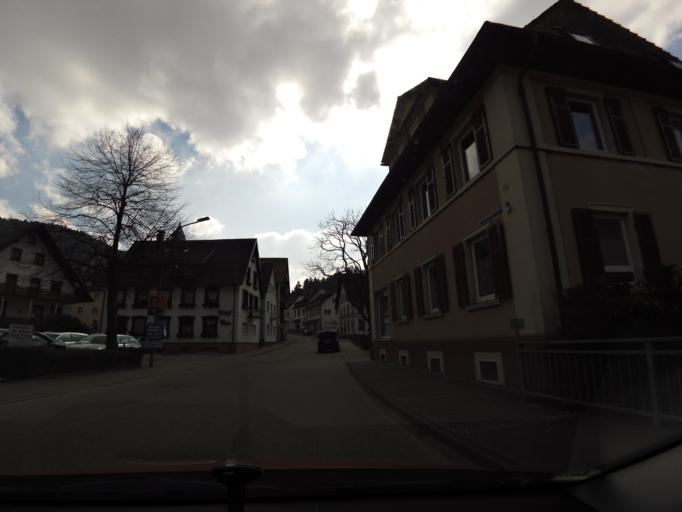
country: DE
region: Baden-Wuerttemberg
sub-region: Freiburg Region
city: Ottenhofen im Schwarzwald
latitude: 48.5674
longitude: 8.1525
